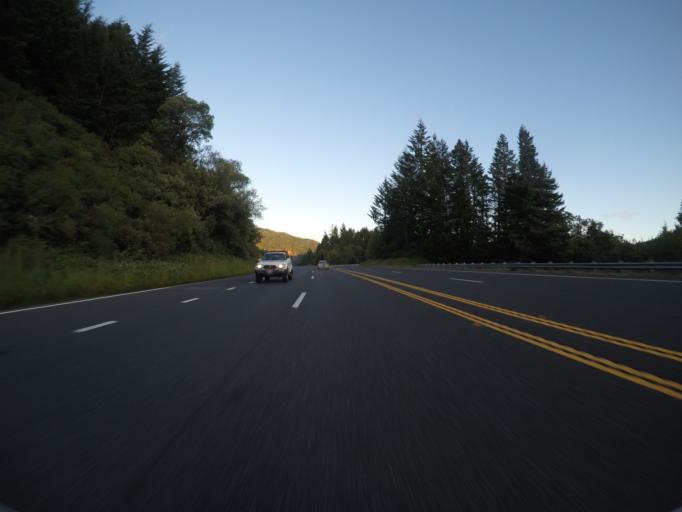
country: US
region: California
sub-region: Humboldt County
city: Redway
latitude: 39.9402
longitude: -123.7774
